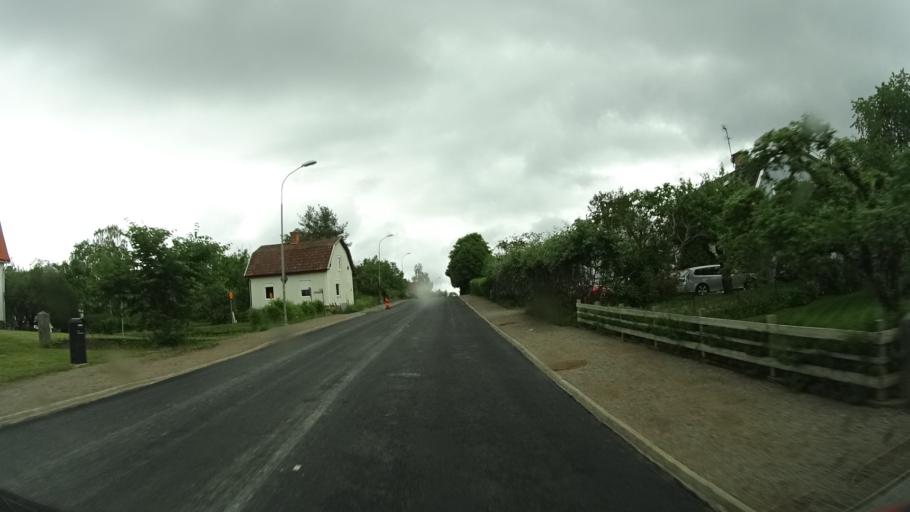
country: SE
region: Kalmar
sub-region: Hogsby Kommun
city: Hoegsby
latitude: 57.4021
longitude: 16.1920
